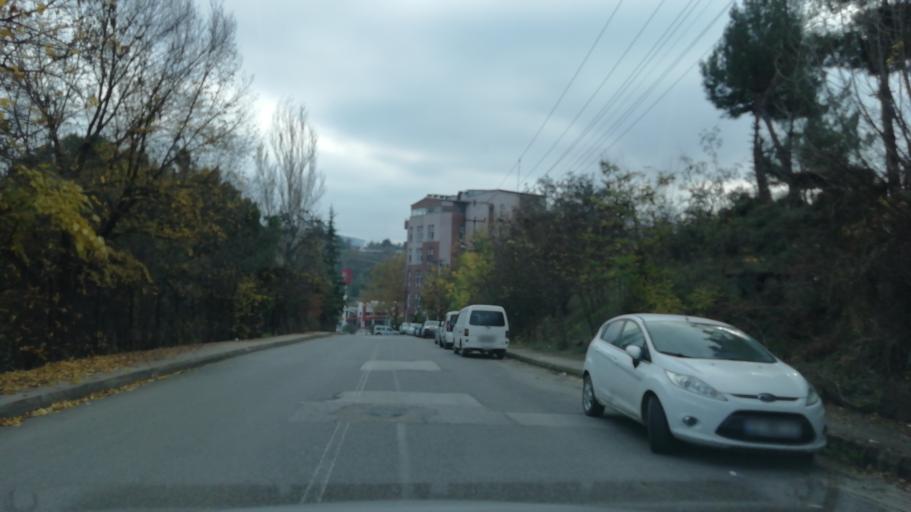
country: TR
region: Karabuk
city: Karabuk
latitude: 41.1983
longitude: 32.6244
